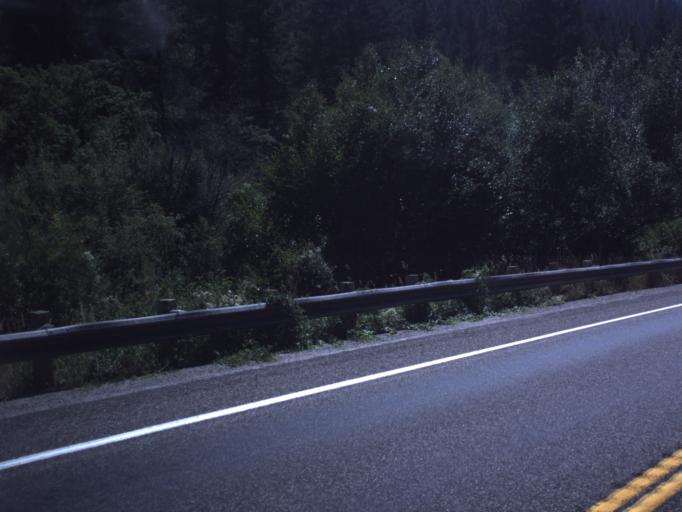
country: US
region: Utah
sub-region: Cache County
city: North Logan
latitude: 41.7784
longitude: -111.6465
